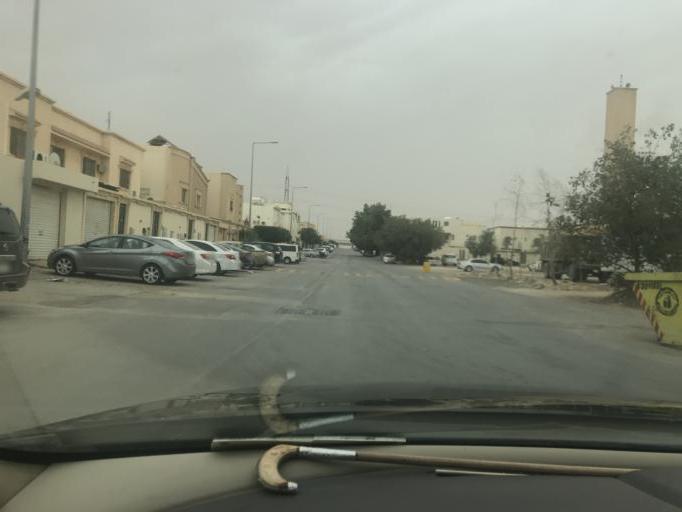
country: SA
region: Ar Riyad
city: Riyadh
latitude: 24.7946
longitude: 46.6926
